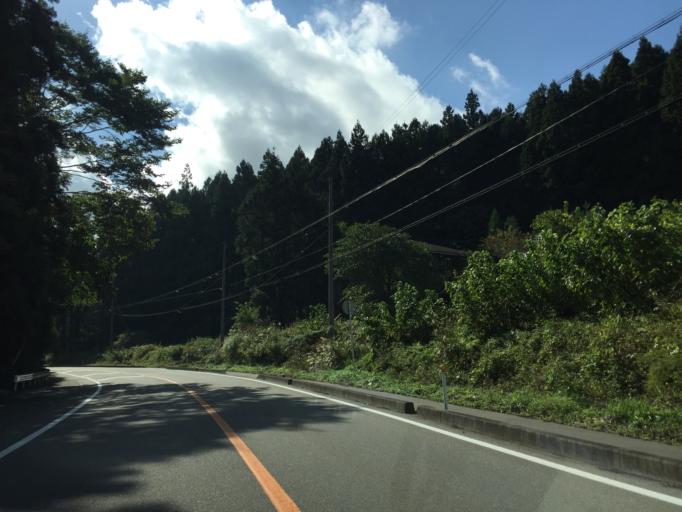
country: JP
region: Fukushima
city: Namie
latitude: 37.5057
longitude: 140.9162
